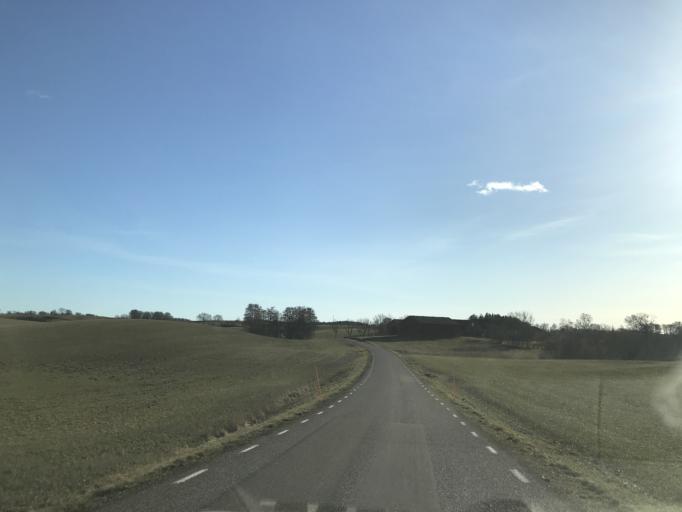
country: SE
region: Skane
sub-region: Ystads Kommun
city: Ystad
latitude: 55.5419
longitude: 13.7883
